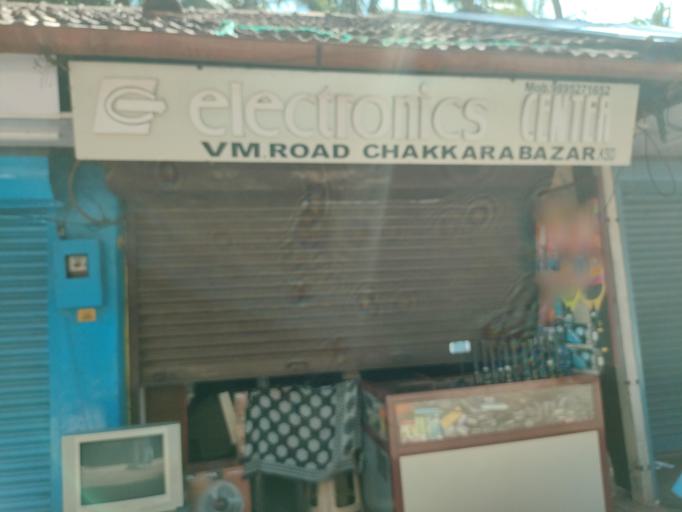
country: IN
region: Kerala
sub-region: Kasaragod District
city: Kasaragod
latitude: 12.5000
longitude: 74.9874
